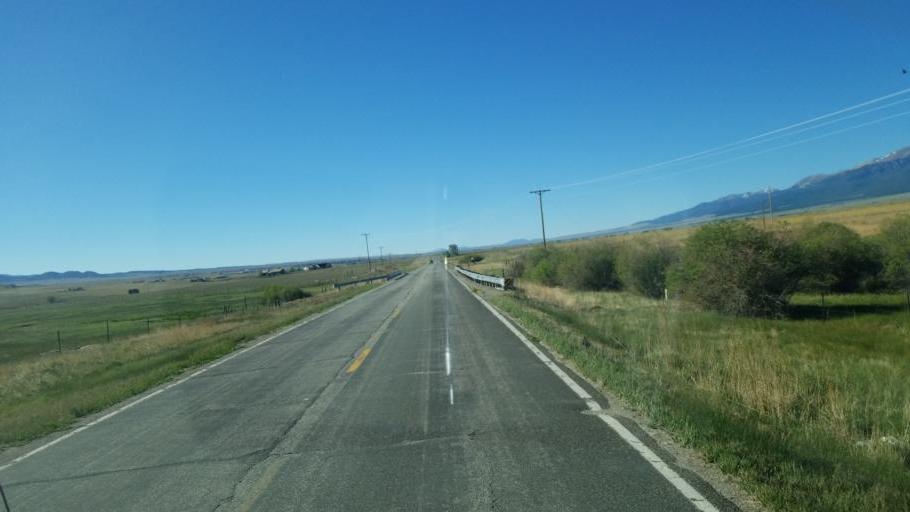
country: US
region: Colorado
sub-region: Custer County
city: Westcliffe
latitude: 38.1808
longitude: -105.5087
